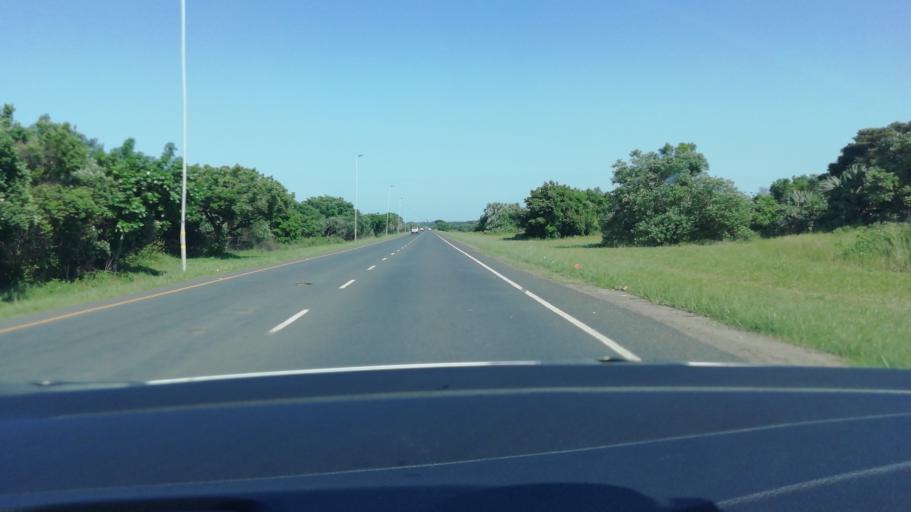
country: ZA
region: KwaZulu-Natal
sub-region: uThungulu District Municipality
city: Richards Bay
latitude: -28.7803
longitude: 32.0802
